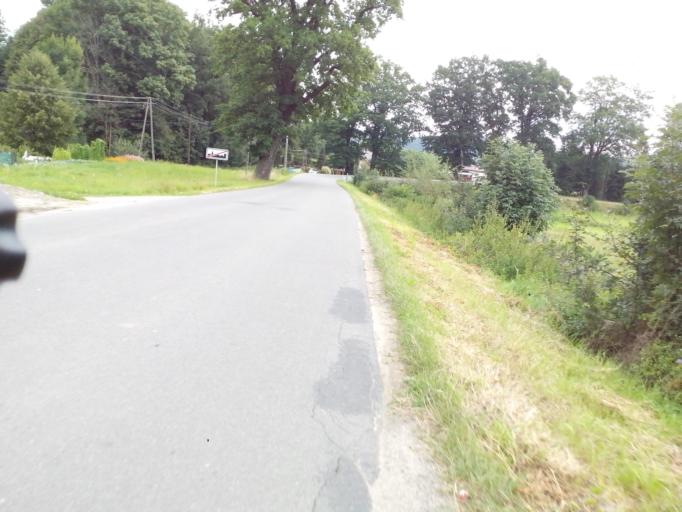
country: PL
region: Subcarpathian Voivodeship
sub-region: Powiat brzozowski
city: Jasienica Rosielna
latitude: 49.7582
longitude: 21.9508
